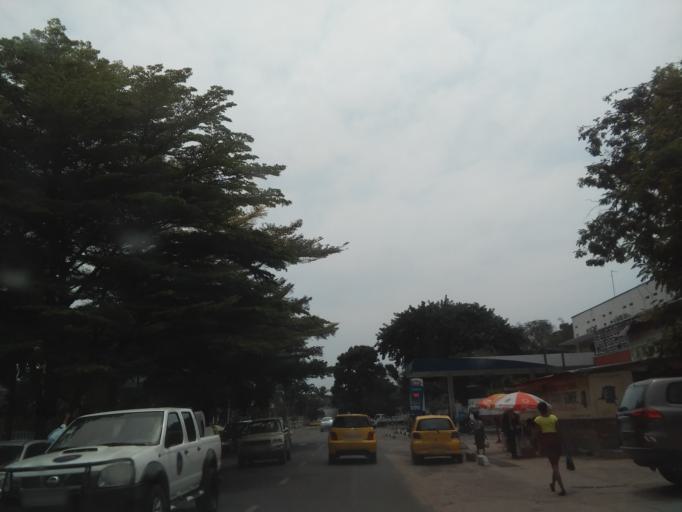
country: CD
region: Kinshasa
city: Kinshasa
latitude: -4.3060
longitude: 15.2938
